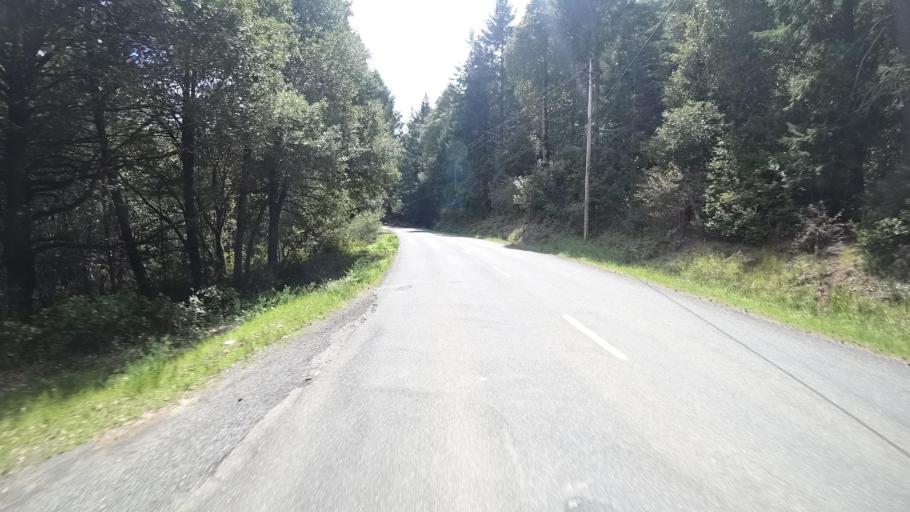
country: US
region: California
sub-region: Humboldt County
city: Redway
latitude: 40.0757
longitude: -123.9572
